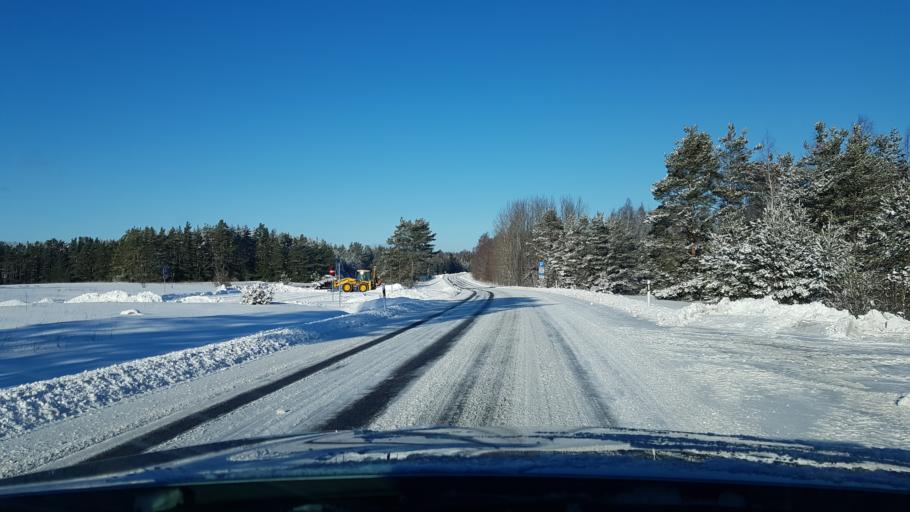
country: EE
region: Hiiumaa
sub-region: Kaerdla linn
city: Kardla
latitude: 58.9581
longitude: 22.7733
